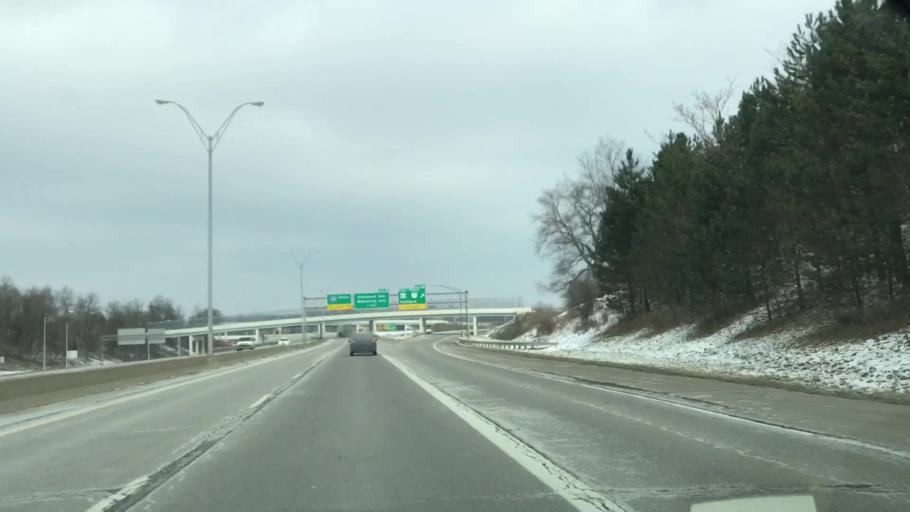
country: US
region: Ohio
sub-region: Mahoning County
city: Youngstown
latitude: 41.0874
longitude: -80.6501
